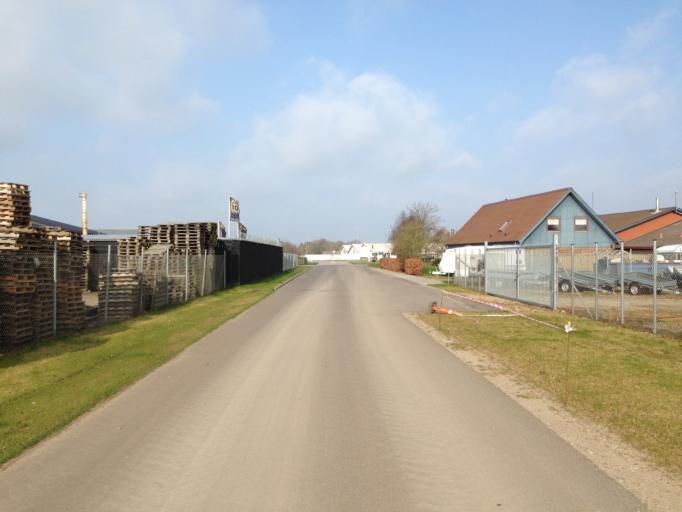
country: DK
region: Central Jutland
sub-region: Herning Kommune
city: Sunds
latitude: 56.1935
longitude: 9.0215
